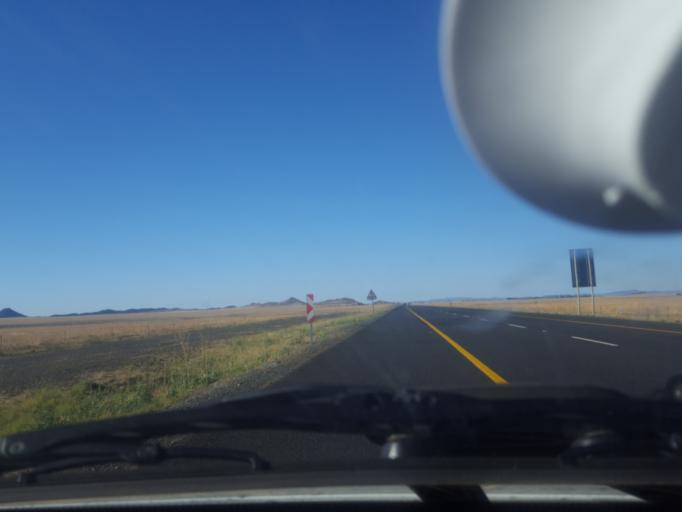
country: ZA
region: Orange Free State
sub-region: Xhariep District Municipality
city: Trompsburg
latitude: -29.8855
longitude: 25.8678
